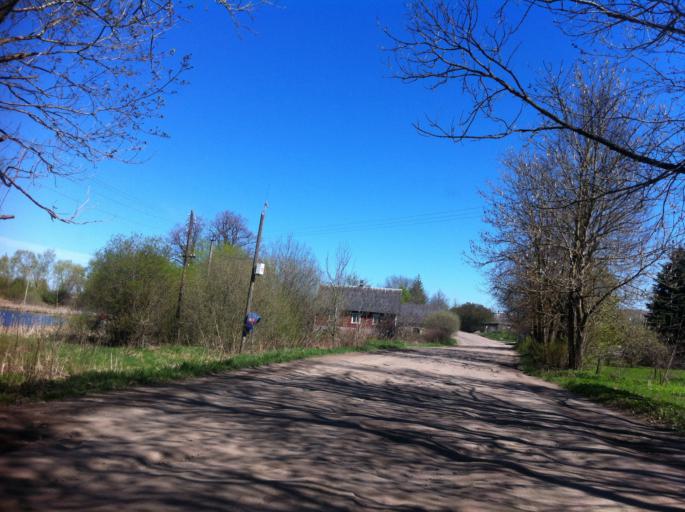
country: RU
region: Pskov
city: Izborsk
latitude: 57.7621
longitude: 27.9545
